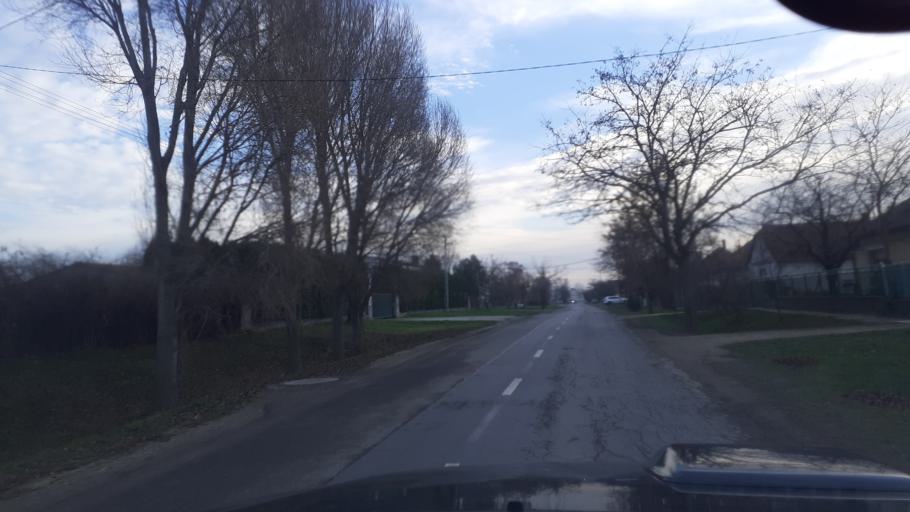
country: HU
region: Bacs-Kiskun
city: Kunszentmiklos
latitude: 47.0166
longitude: 19.1271
